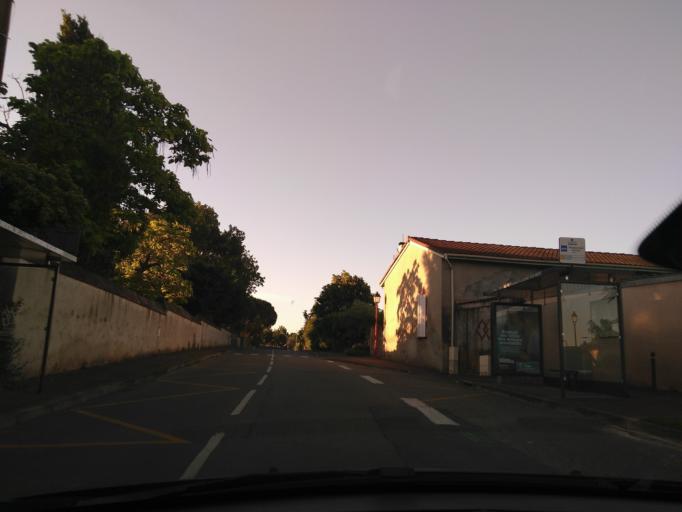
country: FR
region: Midi-Pyrenees
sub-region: Departement de la Haute-Garonne
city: Merville
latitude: 43.7246
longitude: 1.2976
